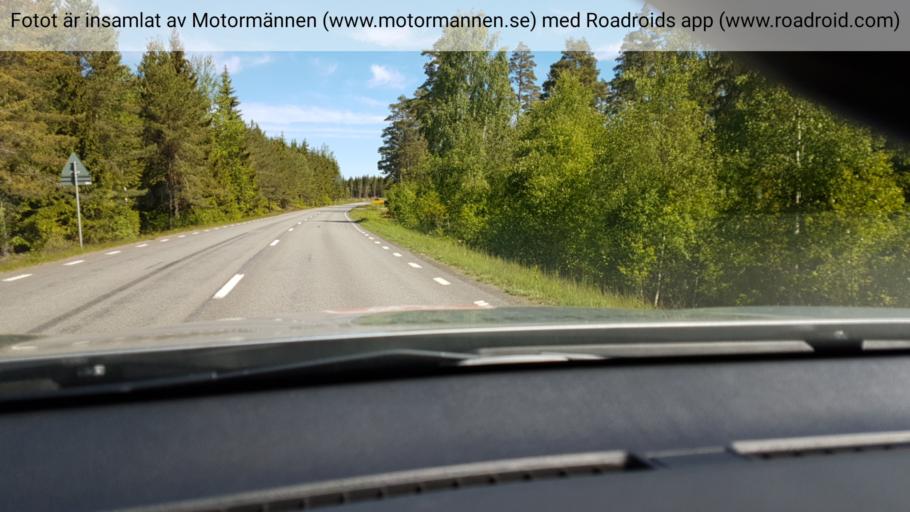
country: SE
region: Vaestra Goetaland
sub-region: Hjo Kommun
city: Hjo
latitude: 58.3890
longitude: 14.3522
